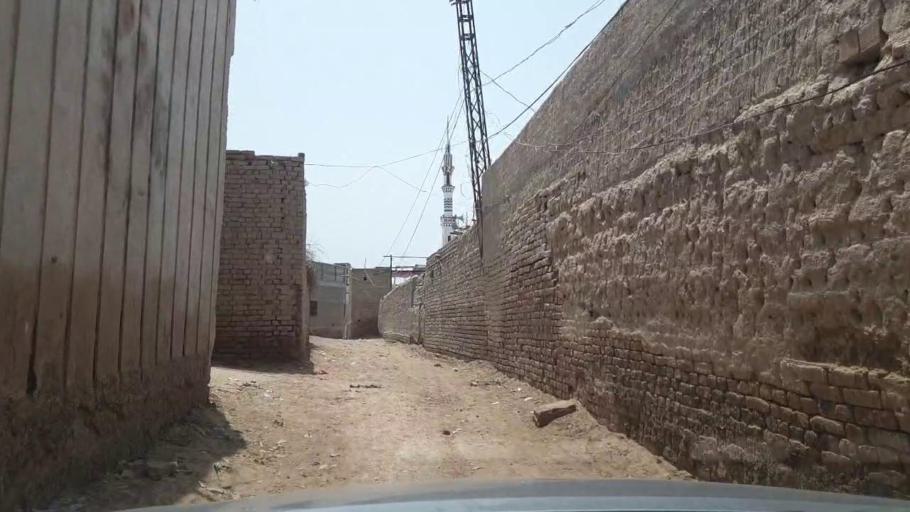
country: PK
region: Sindh
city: Madeji
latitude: 27.7607
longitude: 68.3830
